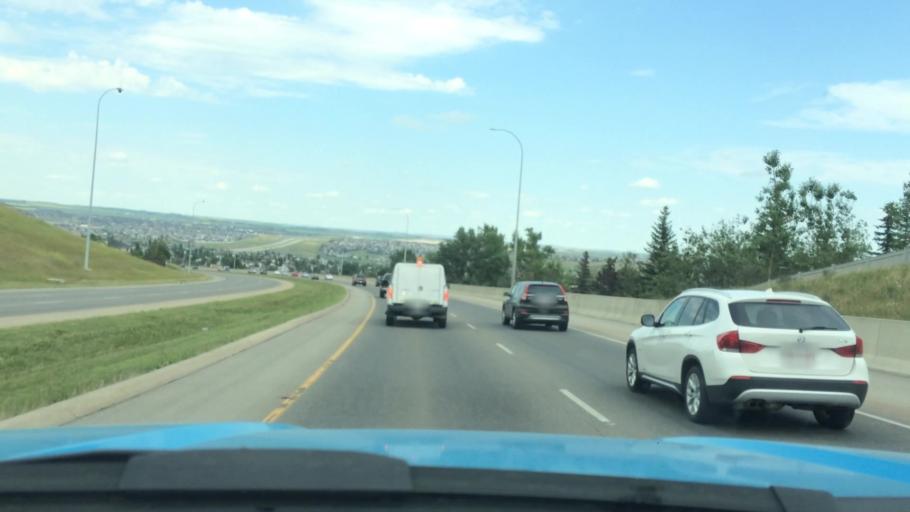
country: CA
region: Alberta
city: Calgary
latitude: 51.1345
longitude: -114.1222
